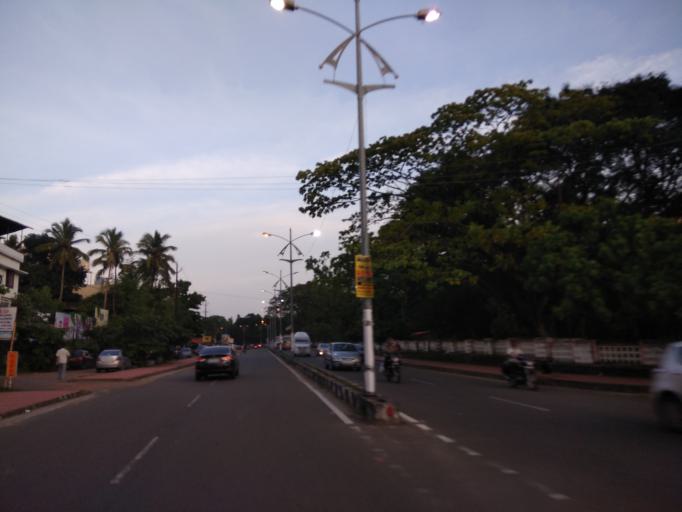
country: IN
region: Kerala
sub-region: Thrissur District
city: Trichur
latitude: 10.5234
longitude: 76.1900
